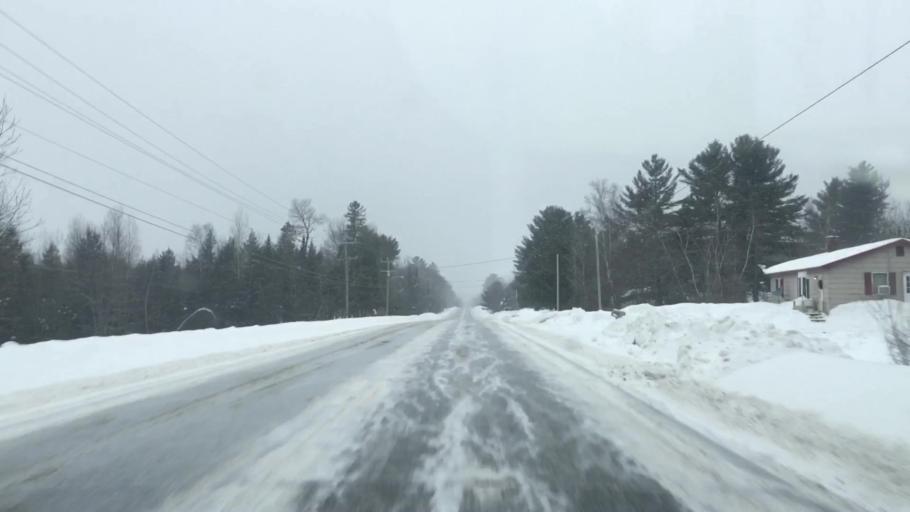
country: US
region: Maine
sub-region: Penobscot County
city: Medway
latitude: 45.5451
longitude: -68.3724
